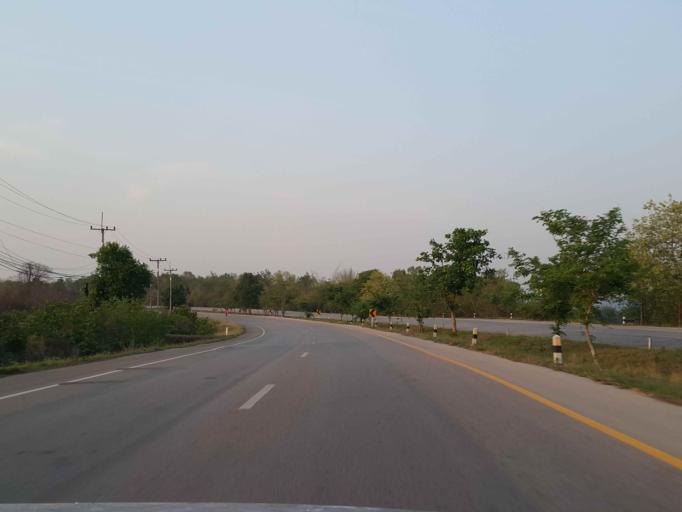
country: TH
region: Lampang
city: Sop Prap
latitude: 17.9576
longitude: 99.3535
